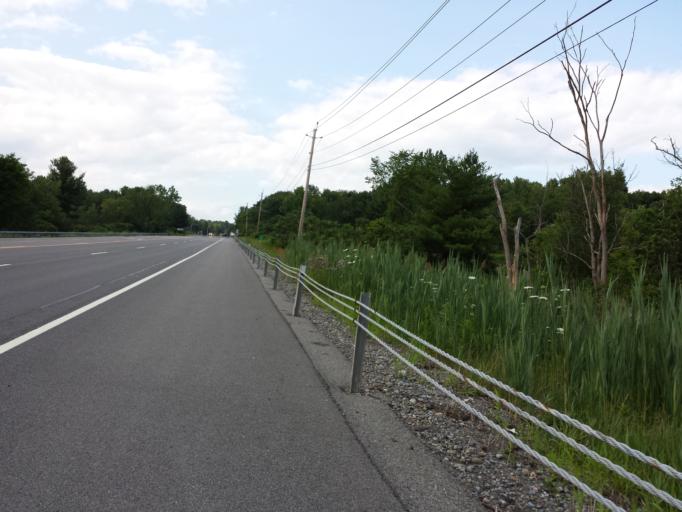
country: US
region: New York
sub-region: Saratoga County
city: Country Knolls
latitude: 42.9434
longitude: -73.7894
